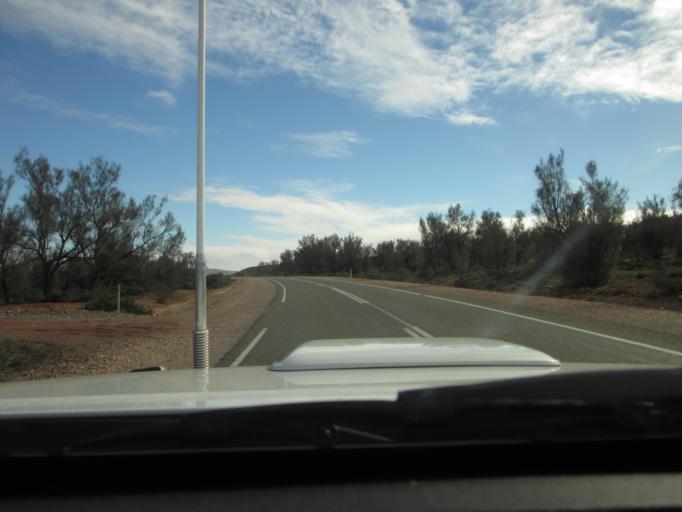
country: AU
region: South Australia
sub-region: Flinders Ranges
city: Quorn
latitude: -31.7865
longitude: 138.3520
